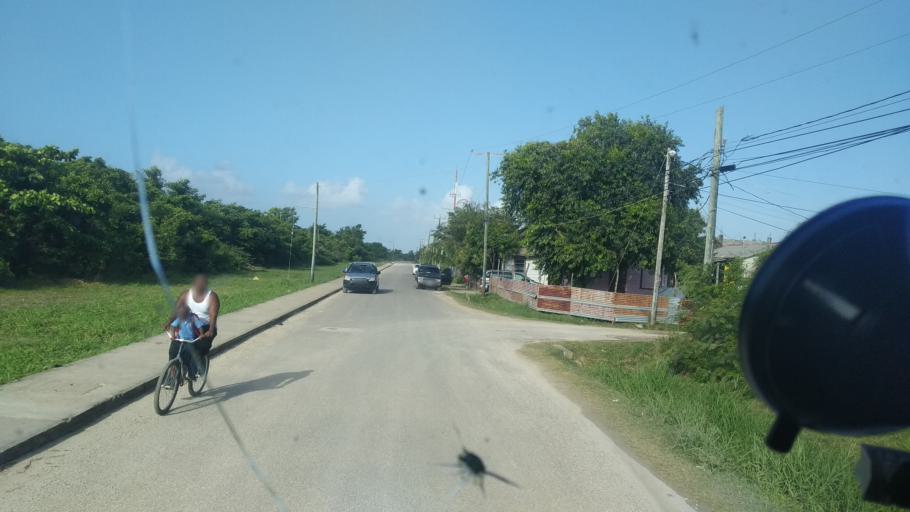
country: BZ
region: Belize
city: Belize City
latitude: 17.4849
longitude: -88.2026
